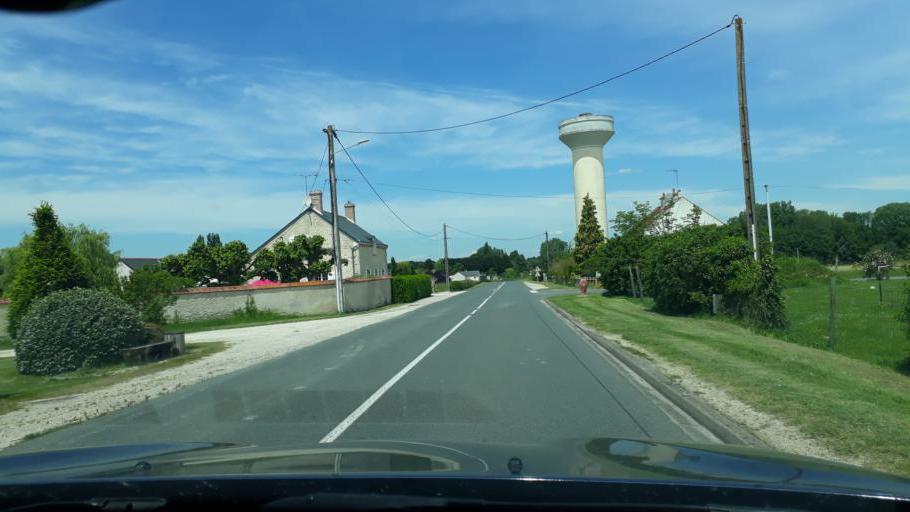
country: FR
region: Centre
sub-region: Departement du Loiret
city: Boynes
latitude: 48.0595
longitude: 2.2899
